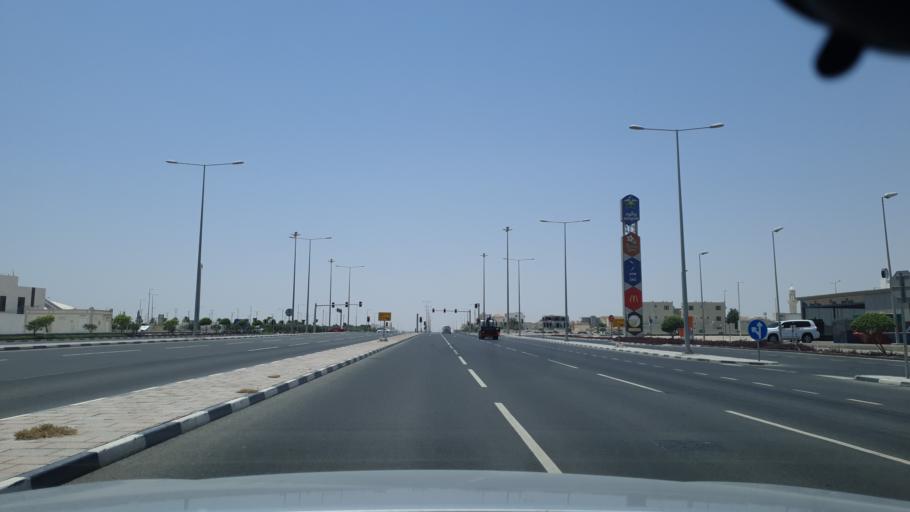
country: QA
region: Baladiyat Umm Salal
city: Umm Salal Muhammad
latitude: 25.3786
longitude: 51.4718
